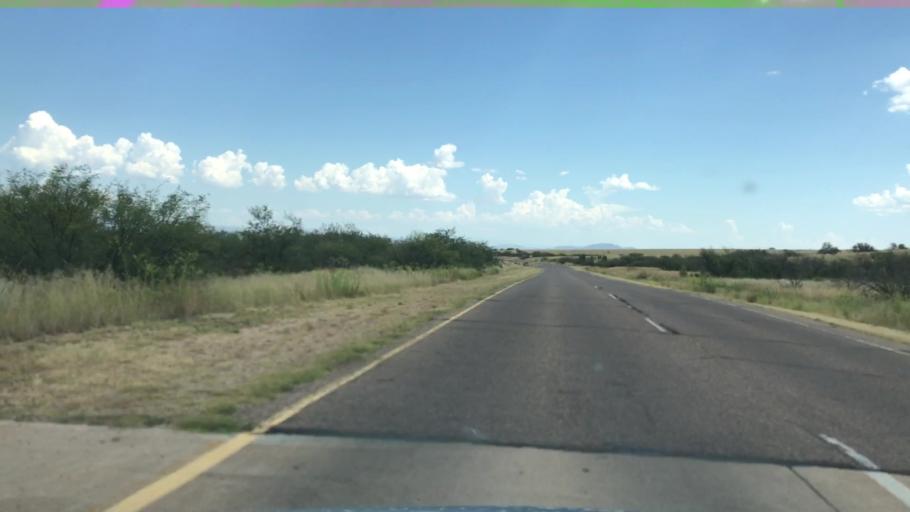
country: US
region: Arizona
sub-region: Cochise County
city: Sierra Vista
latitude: 31.5437
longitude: -110.3306
